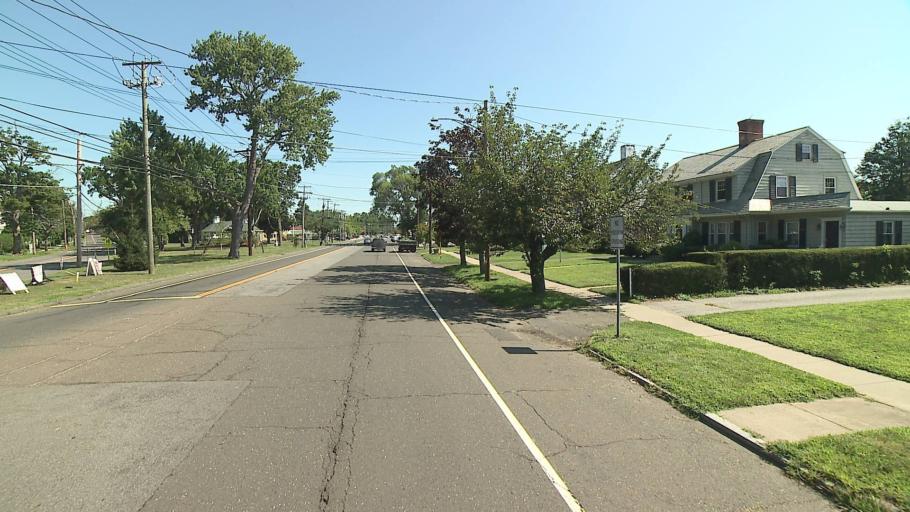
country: US
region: Connecticut
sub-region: Fairfield County
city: Stratford
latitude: 41.2073
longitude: -73.1315
